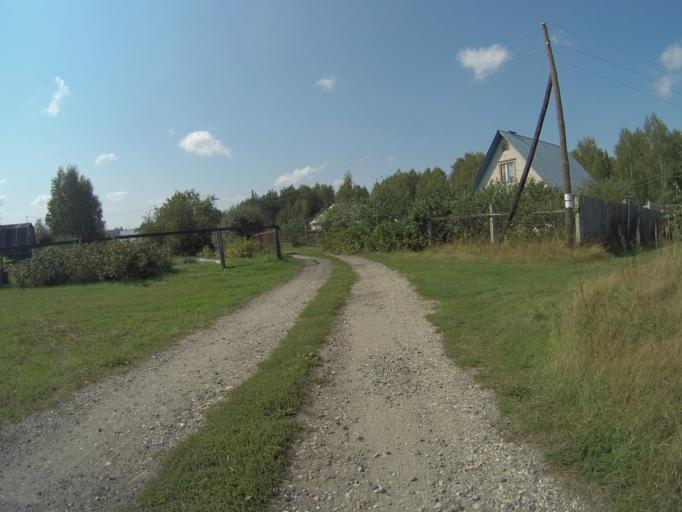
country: RU
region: Vladimir
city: Raduzhnyy
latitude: 55.9950
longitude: 40.2878
